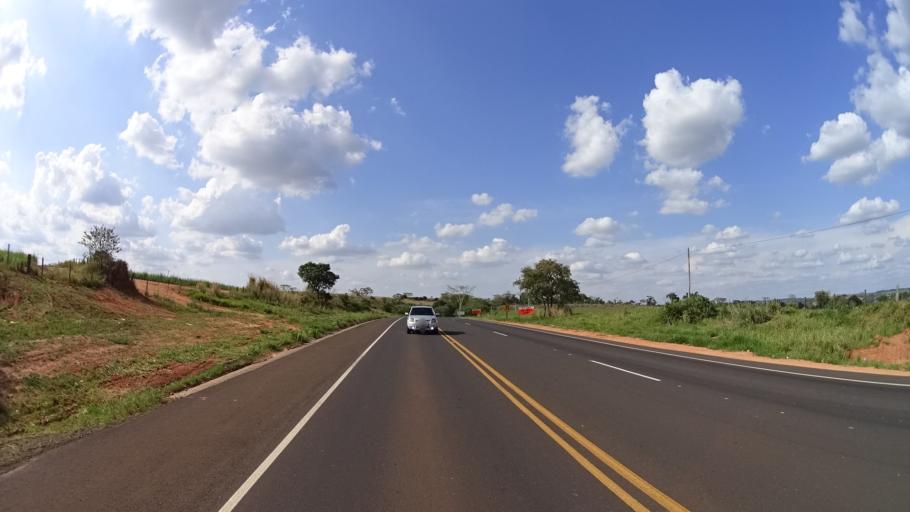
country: BR
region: Sao Paulo
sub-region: Urupes
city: Urupes
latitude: -21.0528
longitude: -49.2484
